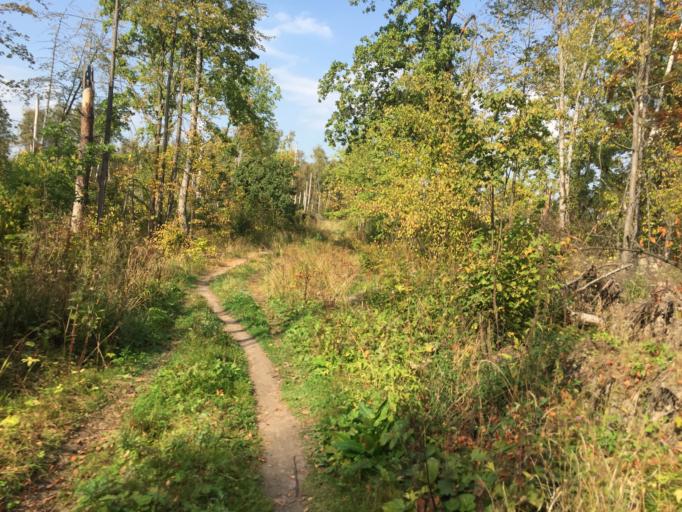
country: RU
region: Moscow
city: Babushkin
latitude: 55.8445
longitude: 37.7443
